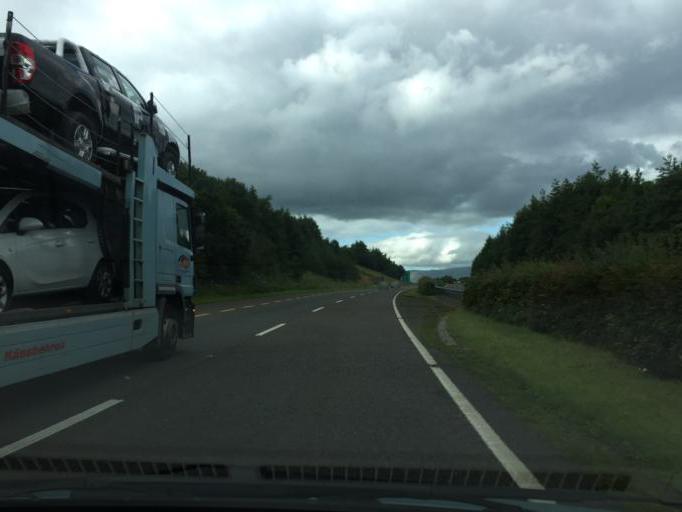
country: IE
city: Ballisodare
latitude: 54.2097
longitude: -8.5023
